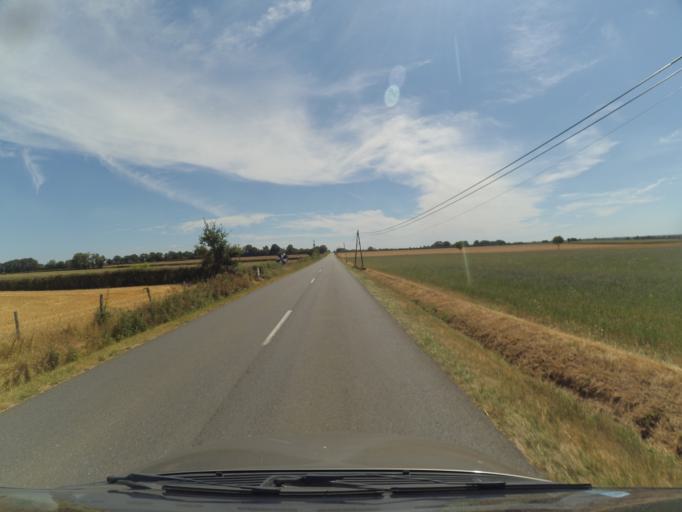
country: FR
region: Poitou-Charentes
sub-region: Departement de la Vienne
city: Usson-du-Poitou
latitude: 46.1795
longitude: 0.5430
